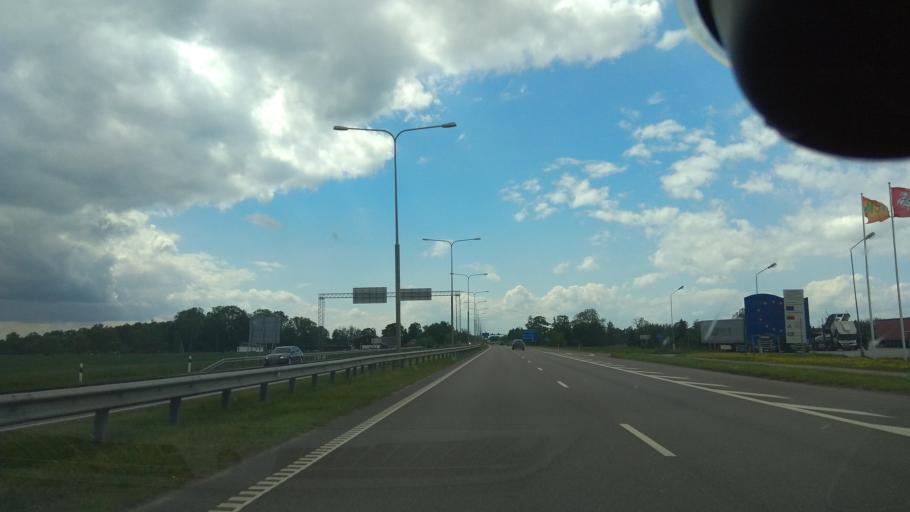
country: LT
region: Marijampoles apskritis
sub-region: Marijampole Municipality
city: Marijampole
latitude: 54.5931
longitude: 23.3909
